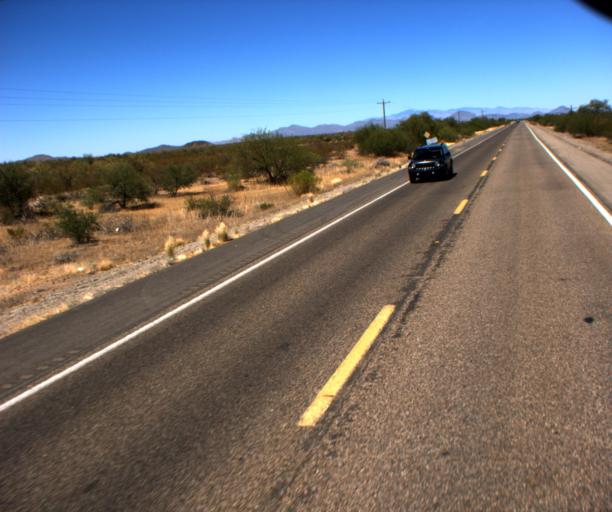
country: US
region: Arizona
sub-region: Pima County
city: Three Points
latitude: 32.0687
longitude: -111.3613
